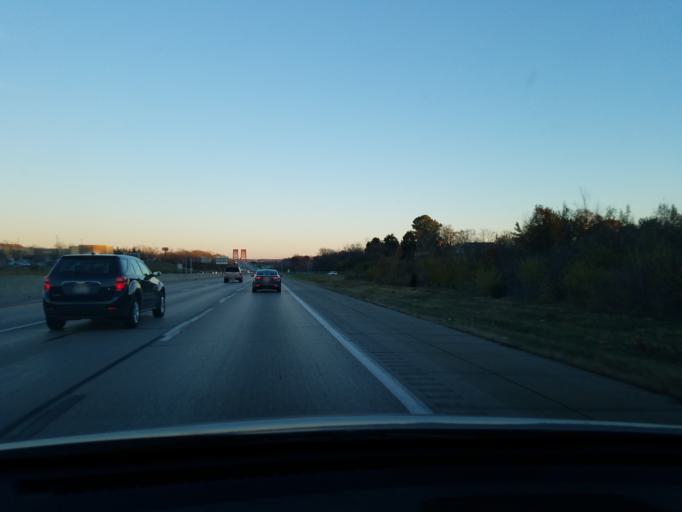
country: US
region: Missouri
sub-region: Saint Louis County
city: Oakville
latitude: 38.4943
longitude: -90.3008
